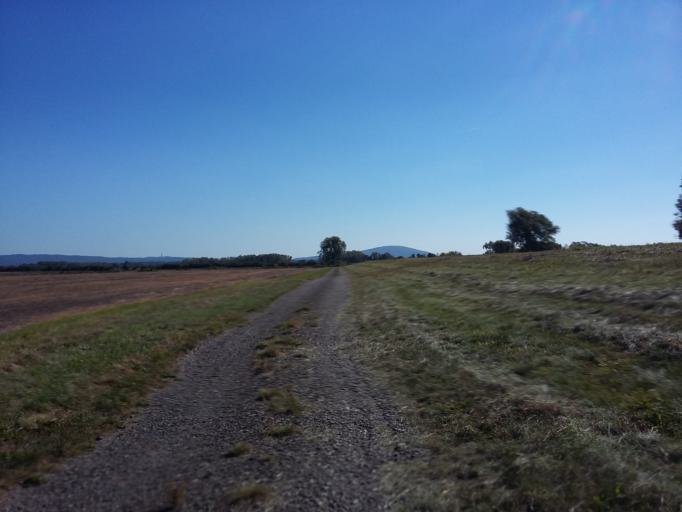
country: AT
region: Lower Austria
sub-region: Politischer Bezirk Ganserndorf
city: Marchegg
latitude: 48.3092
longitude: 16.9236
